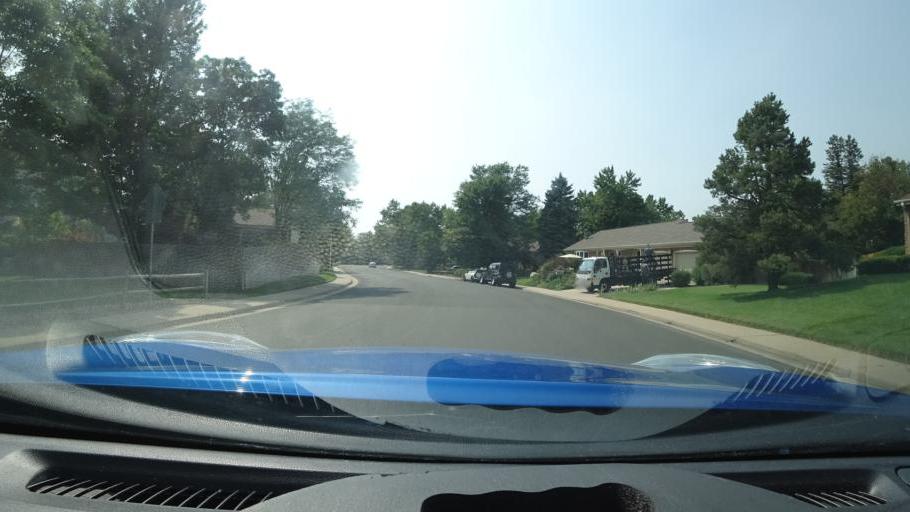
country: US
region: Colorado
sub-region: Adams County
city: Aurora
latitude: 39.6662
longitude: -104.8483
